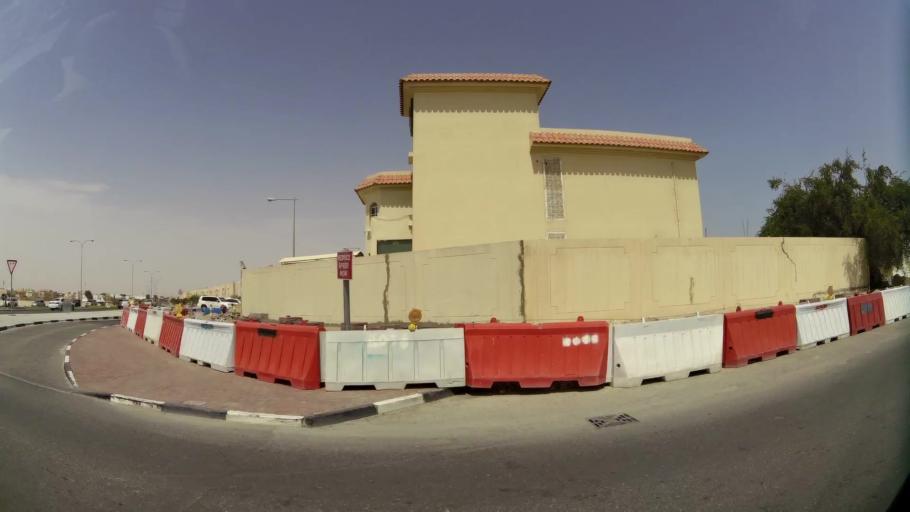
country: QA
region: Baladiyat ad Dawhah
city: Doha
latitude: 25.3245
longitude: 51.4868
